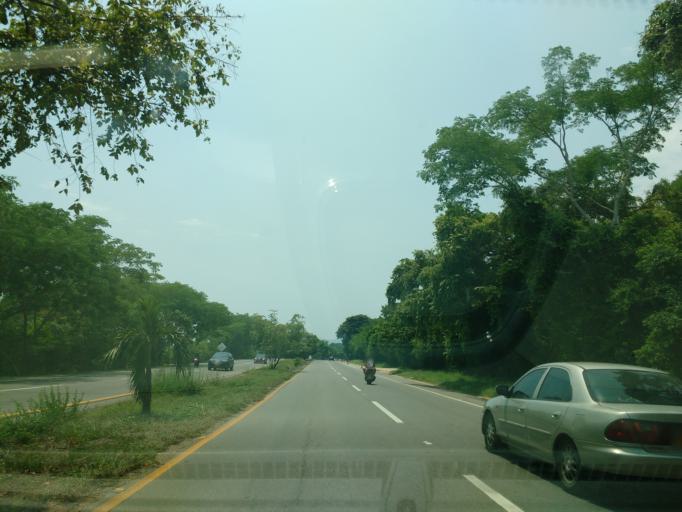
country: CO
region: Tolima
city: Melgar
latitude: 4.2175
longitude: -74.6893
